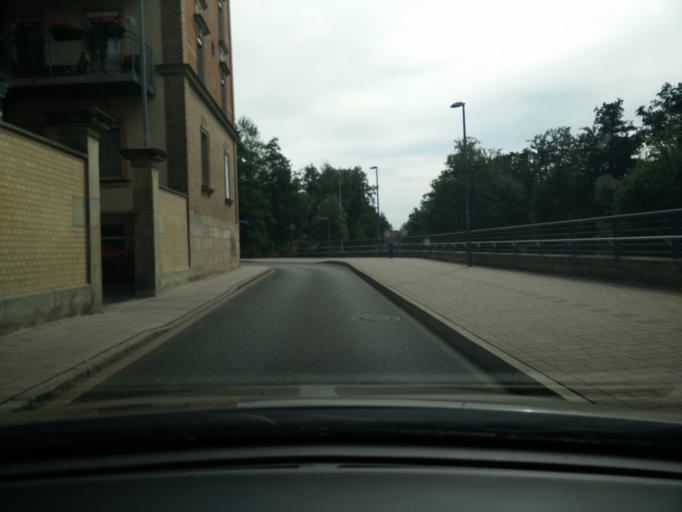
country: DE
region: Bavaria
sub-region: Regierungsbezirk Mittelfranken
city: Furth
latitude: 49.4754
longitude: 10.9810
